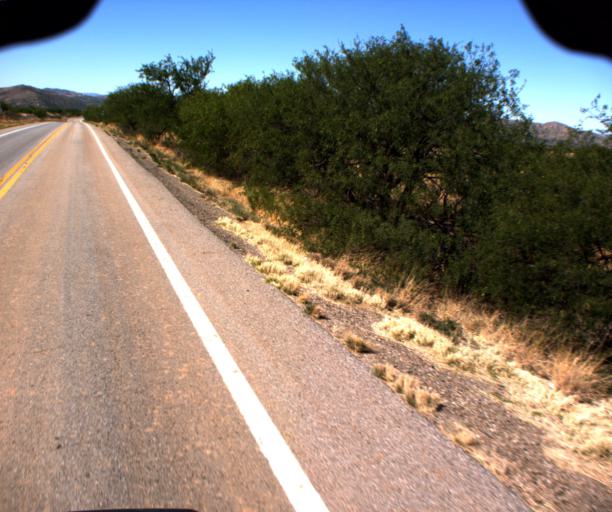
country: US
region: Arizona
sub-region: Santa Cruz County
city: Nogales
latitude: 31.4179
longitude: -110.8524
